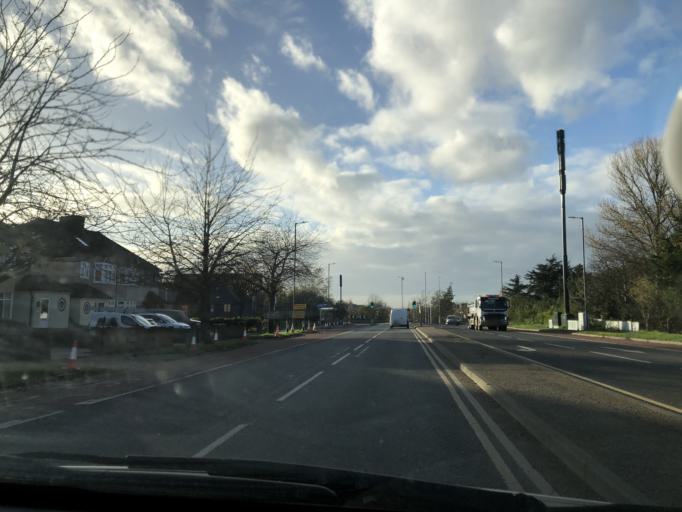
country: GB
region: England
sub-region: Kent
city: Dartford
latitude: 51.4378
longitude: 0.2421
